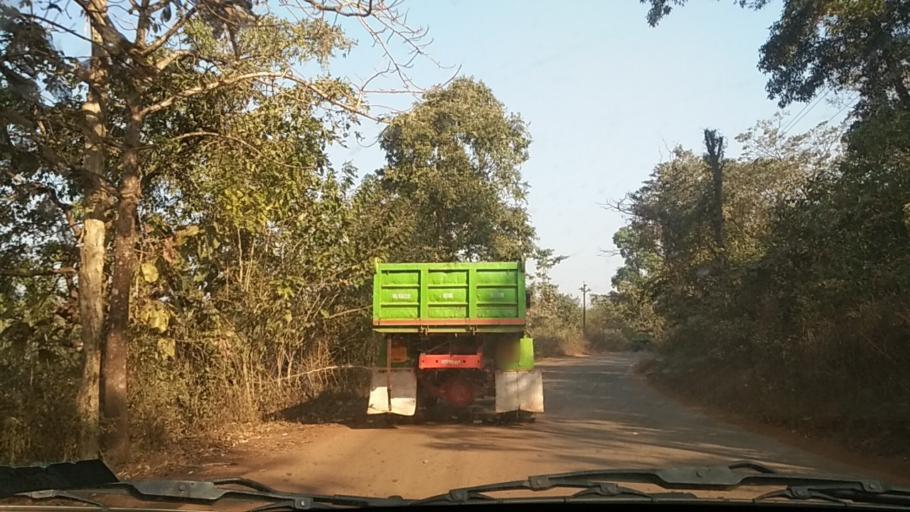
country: IN
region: Goa
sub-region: South Goa
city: Curchorem
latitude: 15.3491
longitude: 74.1196
